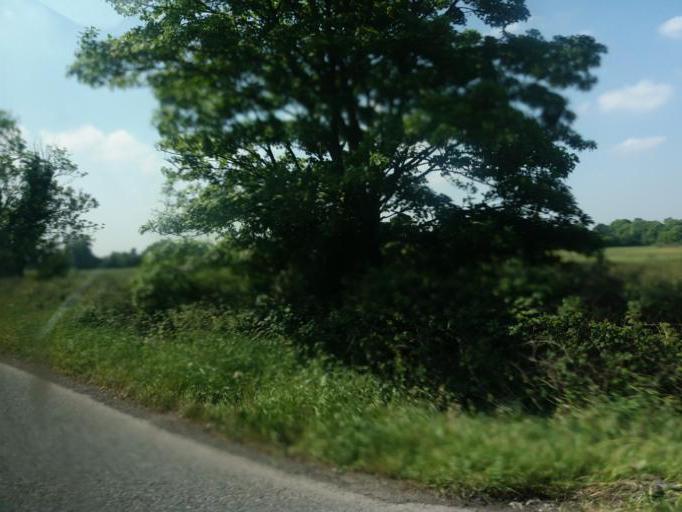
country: IE
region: Leinster
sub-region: An Mhi
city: Ashbourne
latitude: 53.5383
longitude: -6.4256
